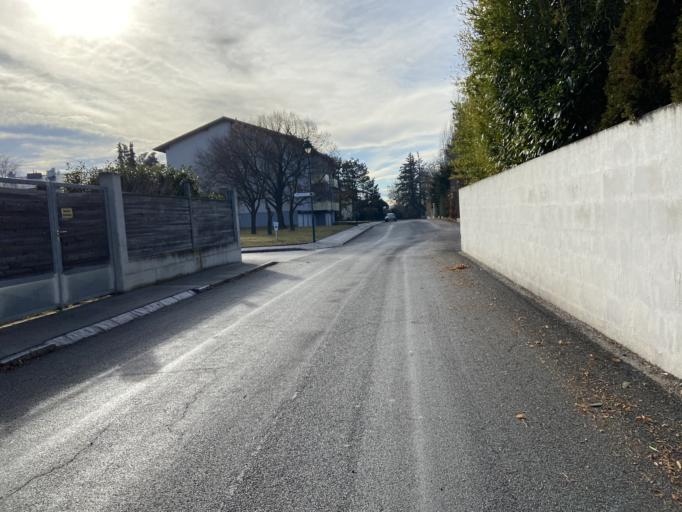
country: AT
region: Lower Austria
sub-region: Politischer Bezirk Modling
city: Laxenburg
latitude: 48.0707
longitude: 16.3482
